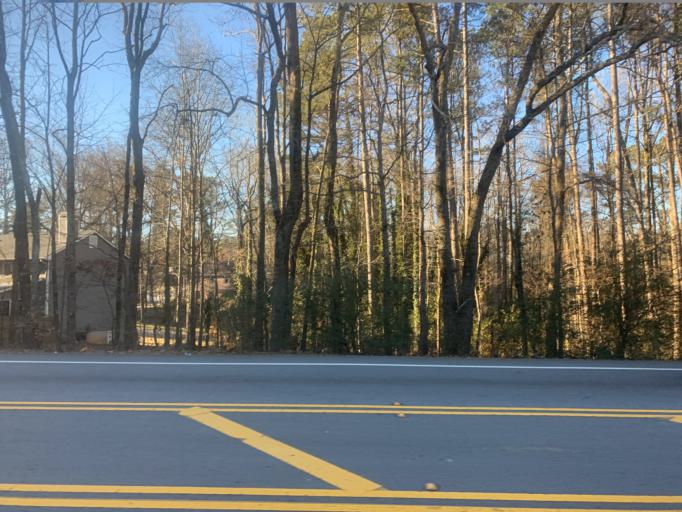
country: US
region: Georgia
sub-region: Gwinnett County
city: Lilburn
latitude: 33.8851
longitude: -84.1196
